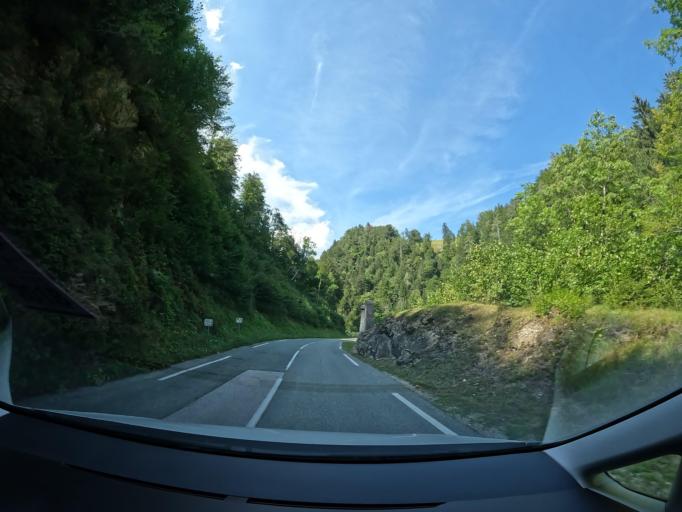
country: SI
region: Trzic
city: Trzic
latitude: 46.3876
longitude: 14.3639
